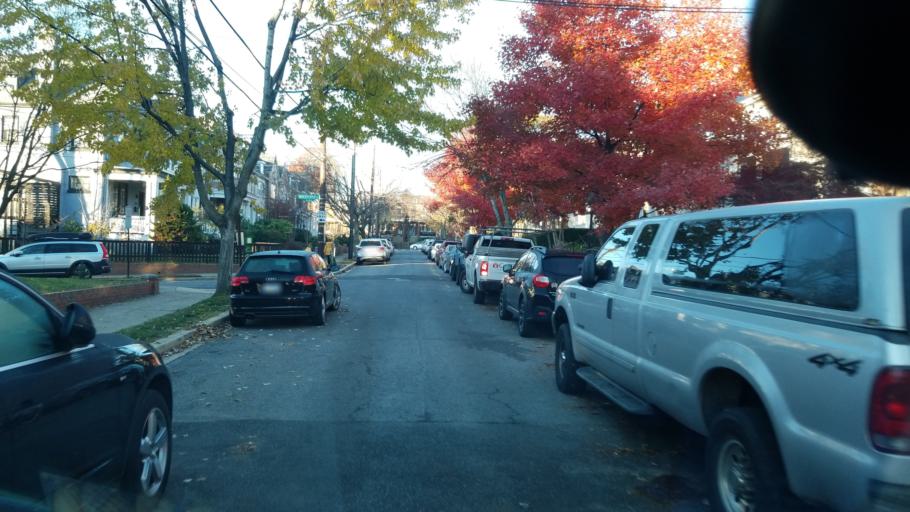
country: US
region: Maryland
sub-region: Montgomery County
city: Friendship Village
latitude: 38.9217
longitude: -77.0757
